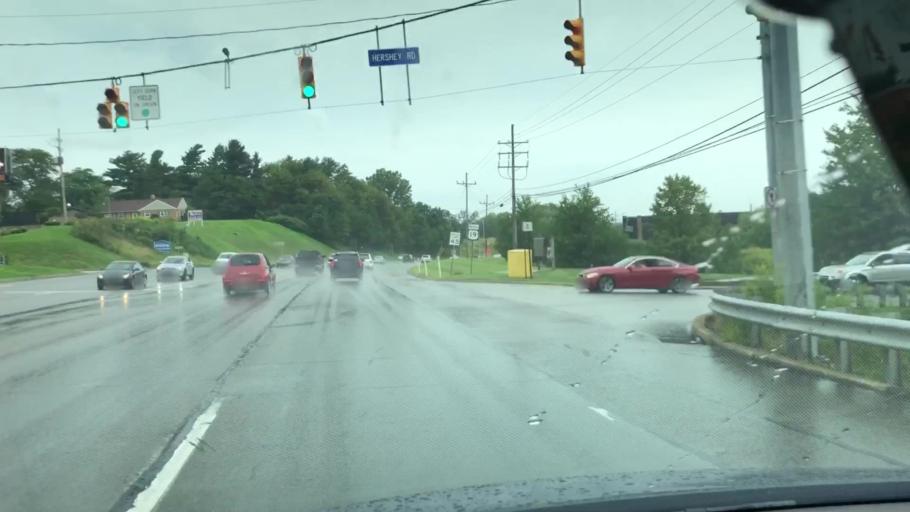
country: US
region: Pennsylvania
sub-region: Erie County
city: Erie
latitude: 42.0590
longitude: -80.0921
